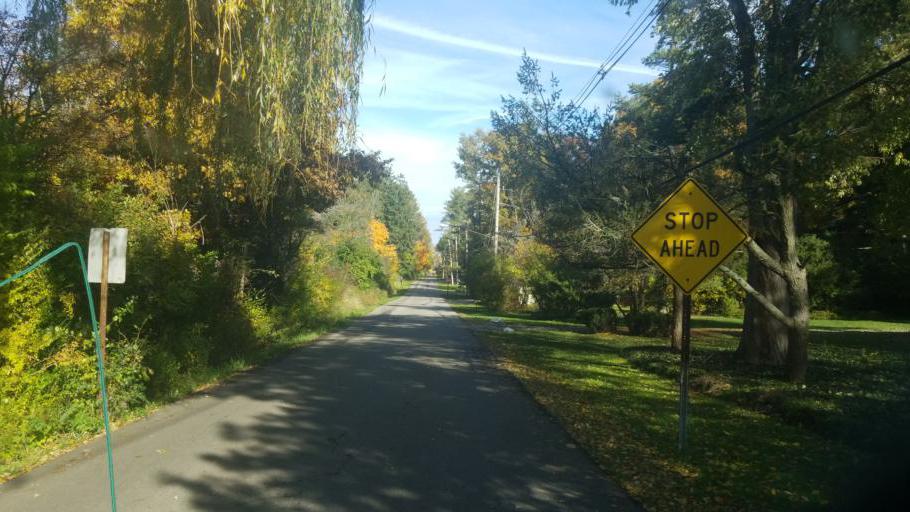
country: US
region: Ohio
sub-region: Richland County
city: Mansfield
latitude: 40.7358
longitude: -82.5421
